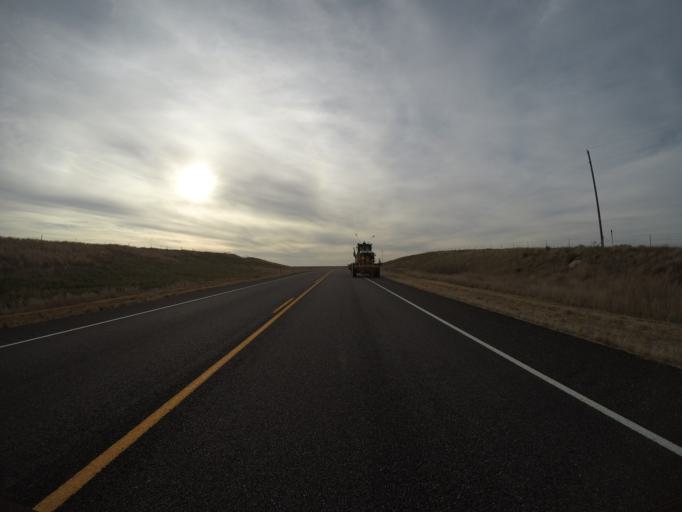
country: US
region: Kansas
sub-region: Cheyenne County
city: Saint Francis
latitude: 39.7468
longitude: -102.0744
